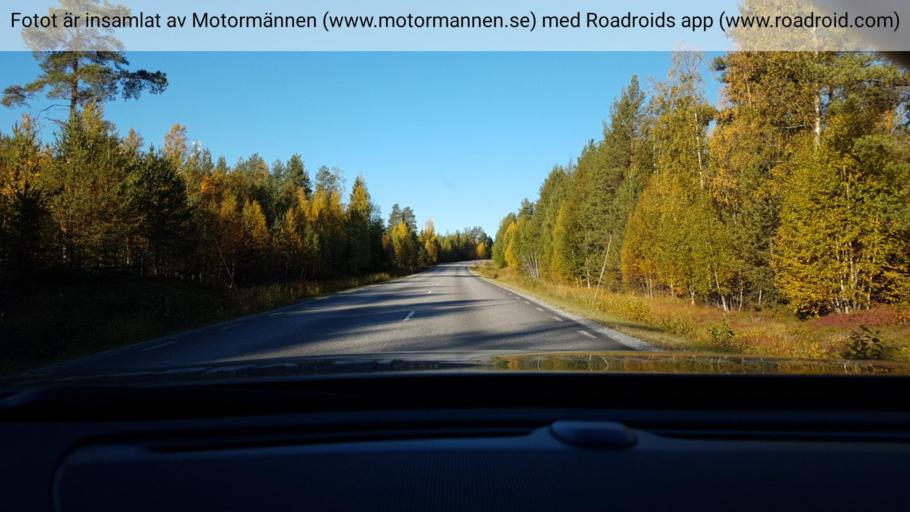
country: SE
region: Norrbotten
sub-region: Pitea Kommun
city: Roknas
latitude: 65.3398
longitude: 21.1610
